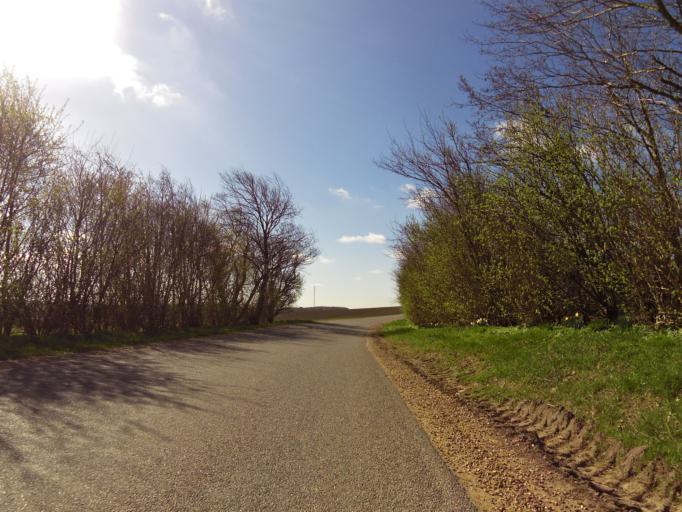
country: DK
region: Central Jutland
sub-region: Holstebro Kommune
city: Vinderup
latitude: 56.4498
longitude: 8.7229
